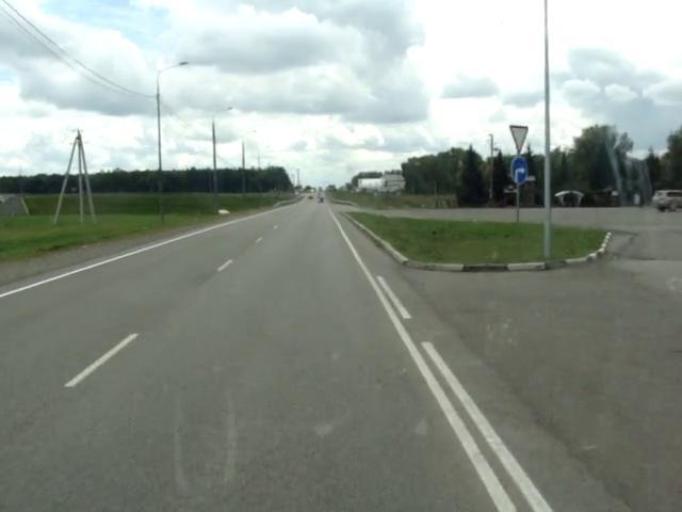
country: RU
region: Altai Krai
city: Zarya
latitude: 52.5795
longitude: 85.1767
